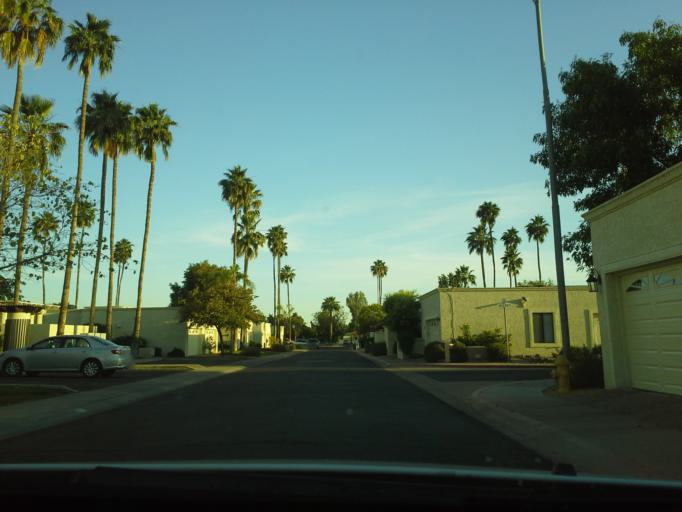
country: US
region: Arizona
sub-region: Maricopa County
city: Phoenix
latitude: 33.5438
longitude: -112.0657
